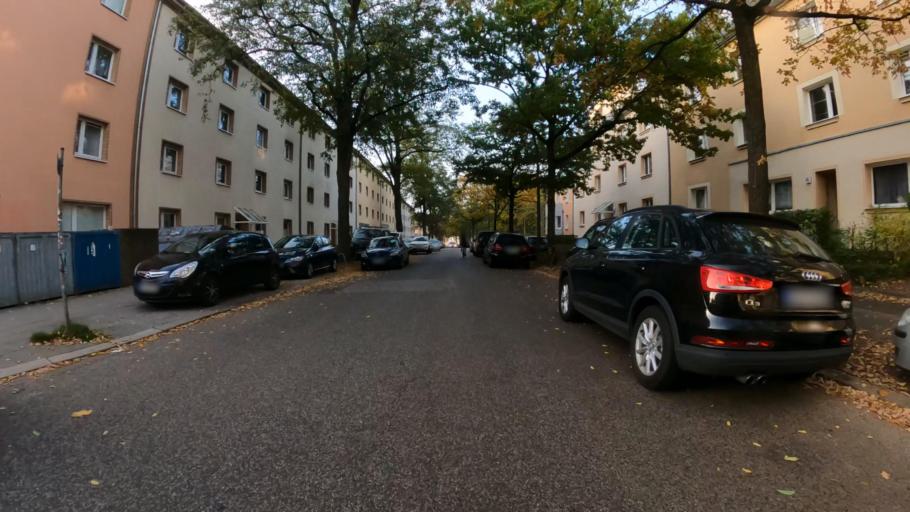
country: DE
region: Hamburg
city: Harburg
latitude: 53.4475
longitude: 9.9924
